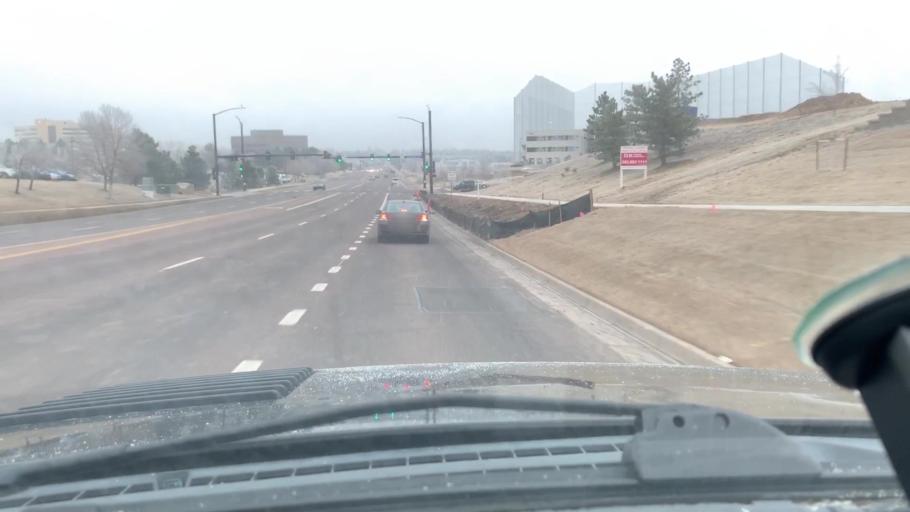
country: US
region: Colorado
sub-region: Arapahoe County
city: Centennial
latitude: 39.5866
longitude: -104.8667
